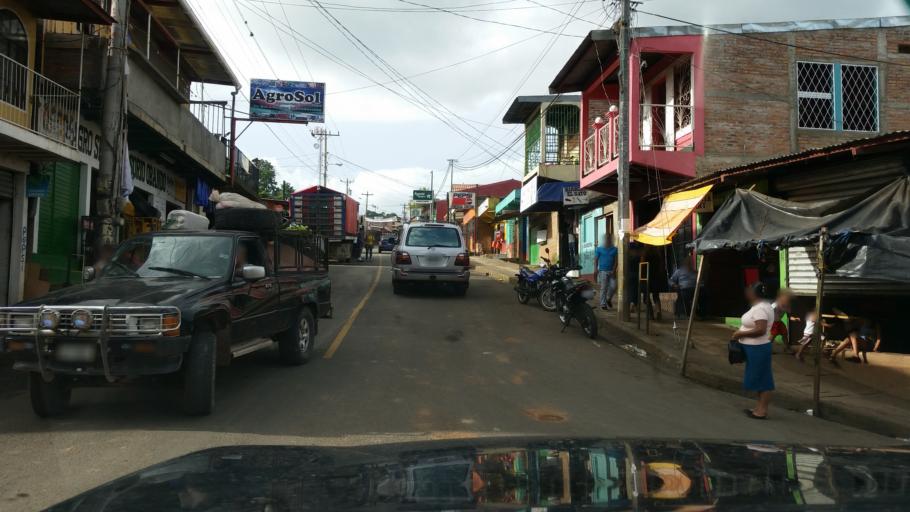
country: NI
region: Matagalpa
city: San Ramon
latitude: 13.1373
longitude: -85.7360
